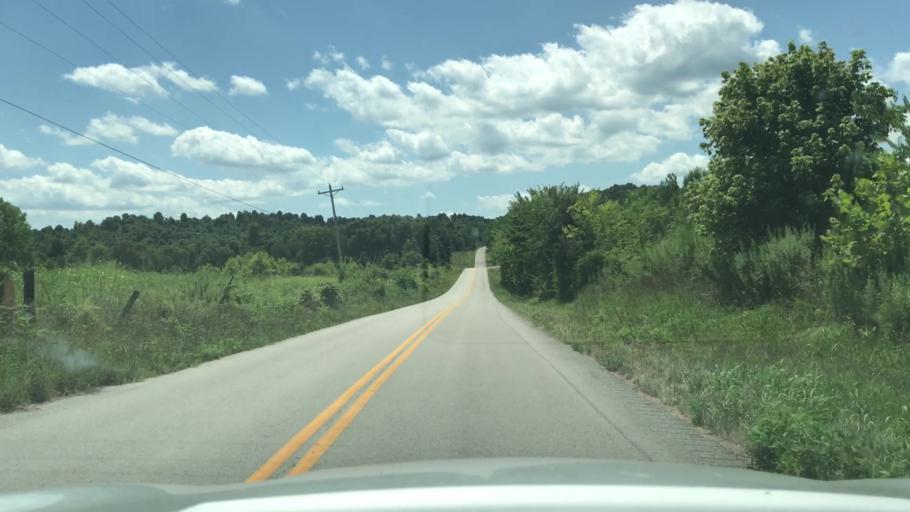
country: US
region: Kentucky
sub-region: Hopkins County
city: Nortonville
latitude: 37.0951
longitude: -87.3417
